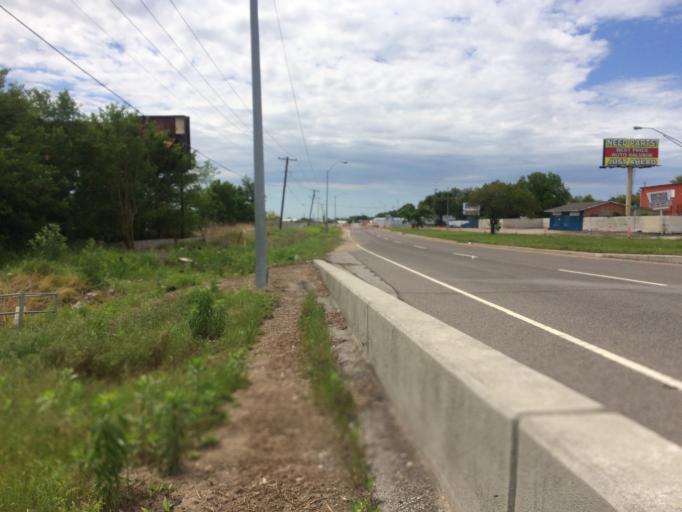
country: US
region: Oklahoma
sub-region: Oklahoma County
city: Oklahoma City
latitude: 35.4566
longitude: -97.5654
